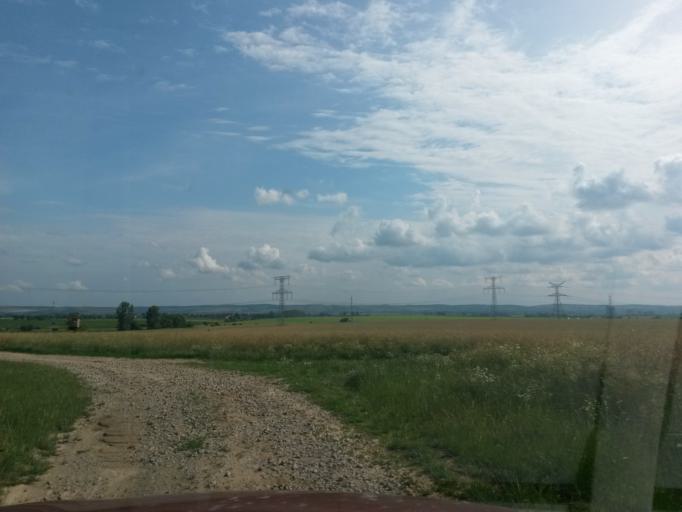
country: SK
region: Kosicky
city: Moldava nad Bodvou
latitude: 48.6100
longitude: 21.1020
